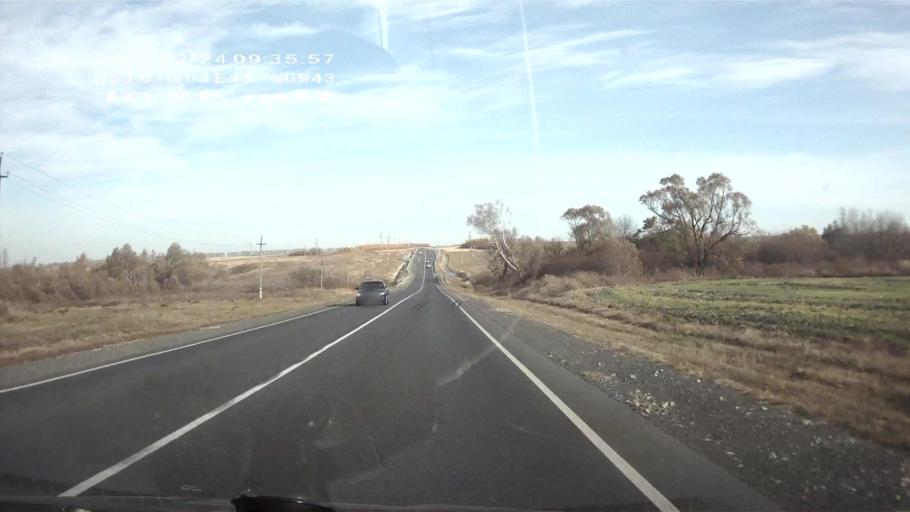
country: RU
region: Penza
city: Mokshan
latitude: 53.6116
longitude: 44.7310
